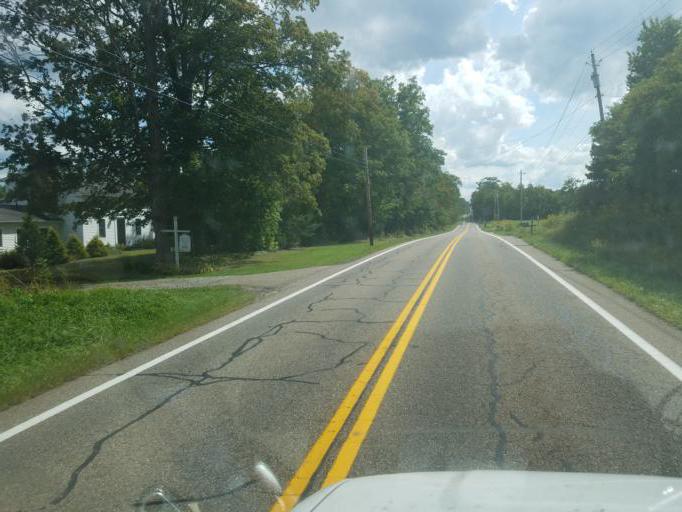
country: US
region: Ohio
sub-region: Portage County
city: Hiram
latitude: 41.3255
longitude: -81.1432
